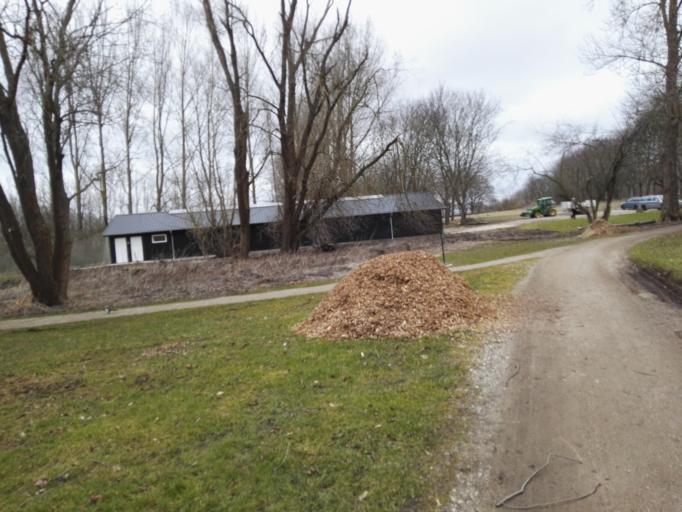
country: DK
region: Capital Region
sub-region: Ballerup Kommune
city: Ballerup
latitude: 55.7133
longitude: 12.3713
